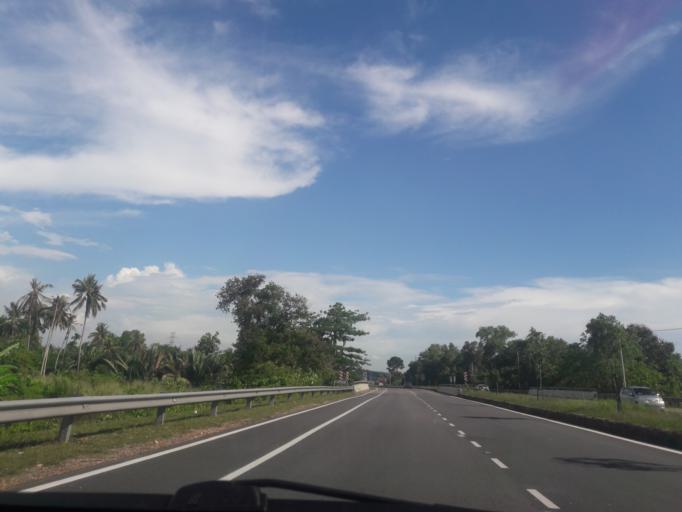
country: MY
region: Kedah
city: Sungai Petani
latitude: 5.6214
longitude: 100.4648
